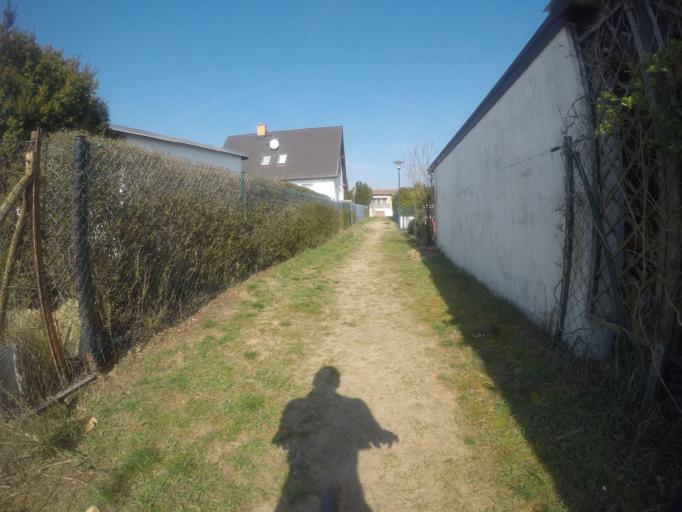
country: DE
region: Berlin
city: Muggelheim
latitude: 52.3896
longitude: 13.7107
